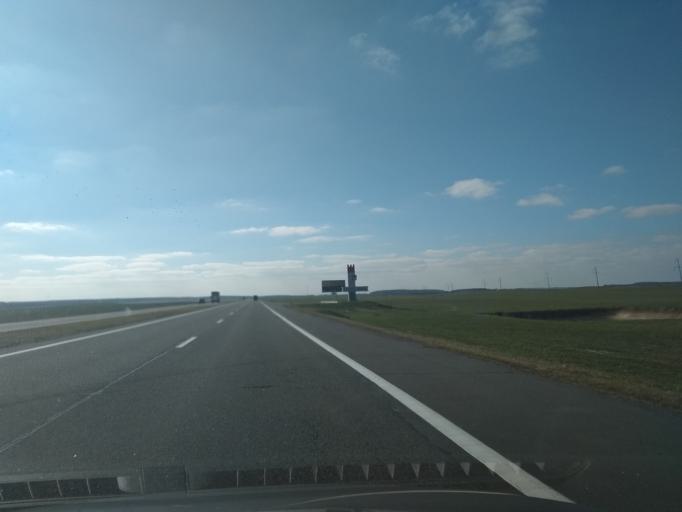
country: BY
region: Minsk
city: Snow
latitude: 53.3162
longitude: 26.3999
